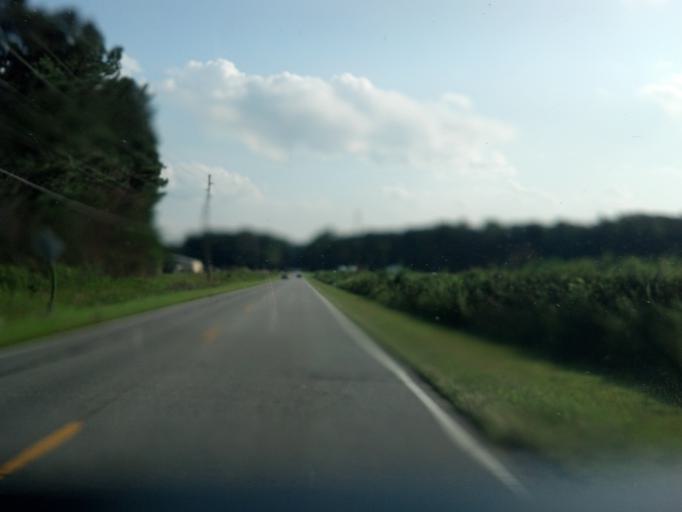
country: US
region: North Carolina
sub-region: Pitt County
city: Ayden
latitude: 35.4991
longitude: -77.4141
